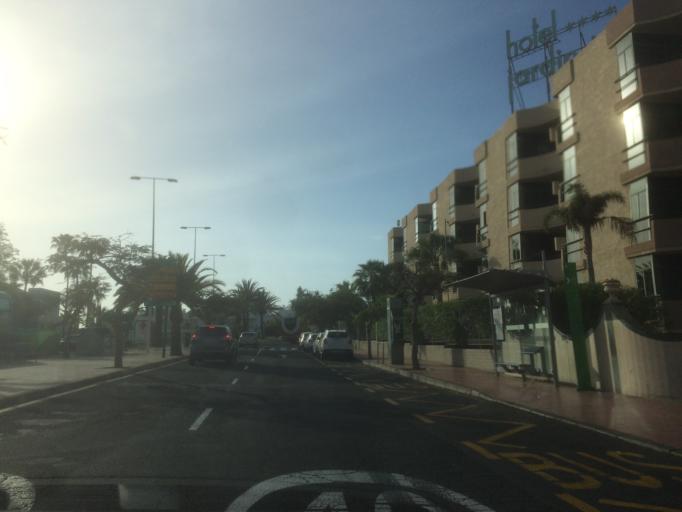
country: ES
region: Canary Islands
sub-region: Provincia de Santa Cruz de Tenerife
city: Playa de las Americas
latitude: 28.0888
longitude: -16.7342
